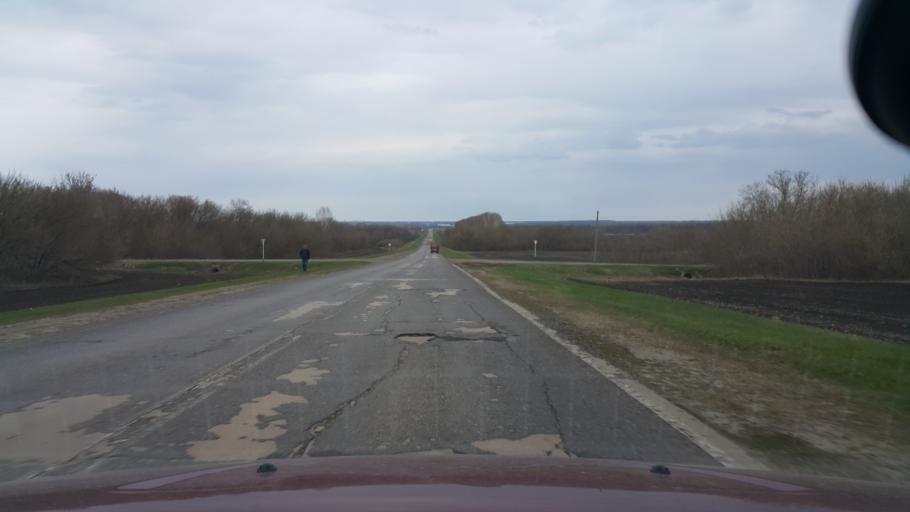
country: RU
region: Tambov
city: Bokino
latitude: 52.5733
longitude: 41.4238
